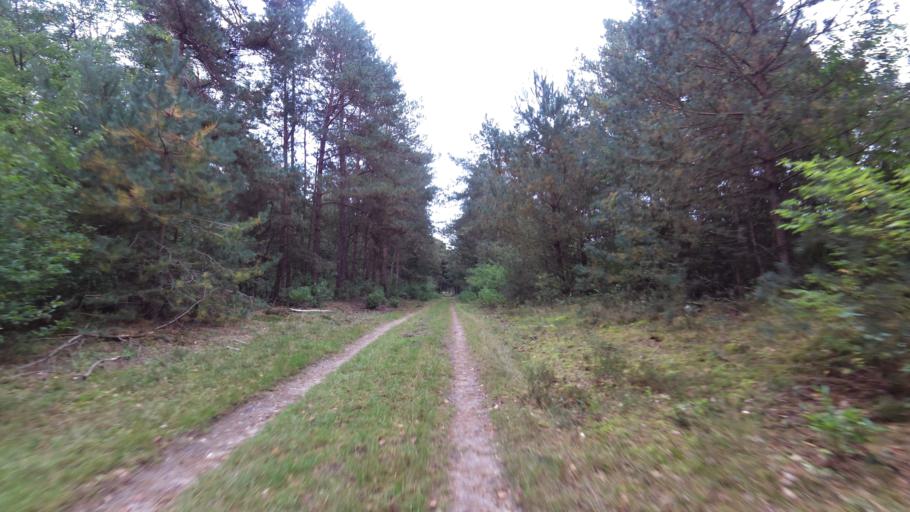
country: NL
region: Gelderland
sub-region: Gemeente Apeldoorn
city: Uddel
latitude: 52.1988
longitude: 5.8100
